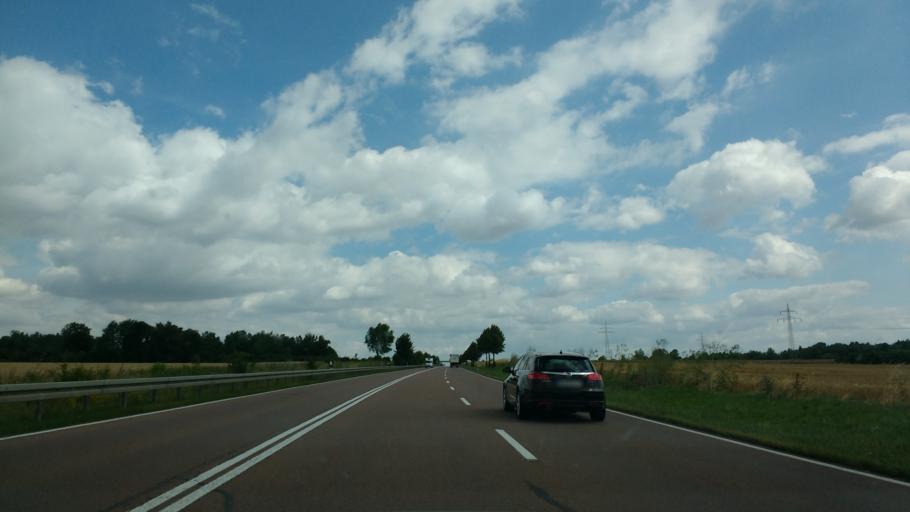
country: DE
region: Saxony-Anhalt
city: Theissen
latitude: 51.0626
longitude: 12.1021
